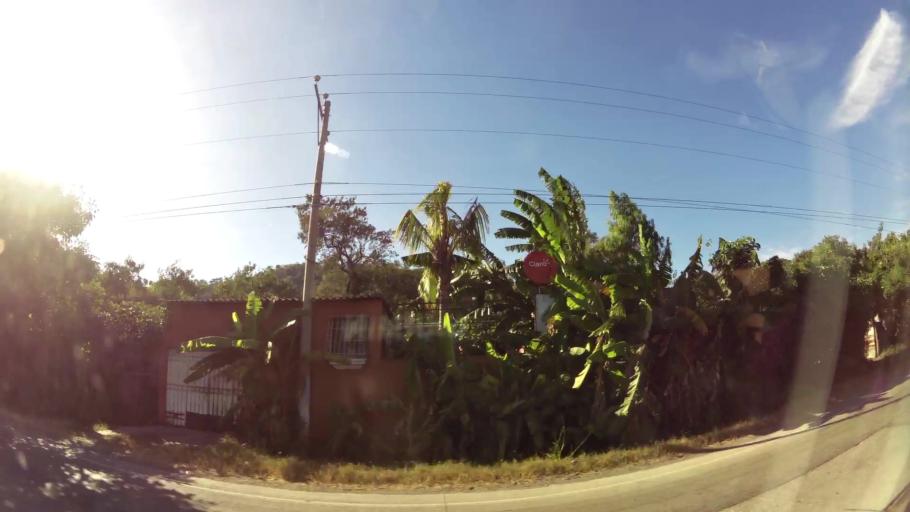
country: SV
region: Santa Ana
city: Santa Ana
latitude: 14.0379
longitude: -89.5218
